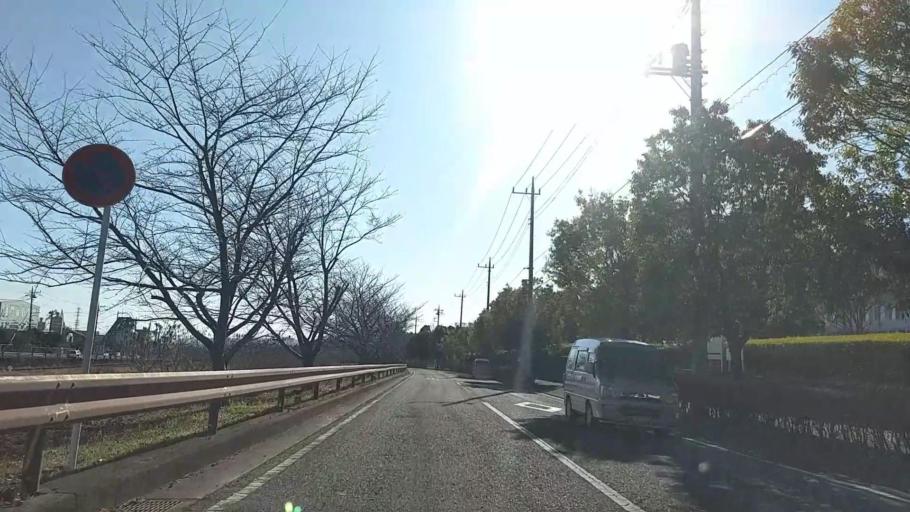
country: JP
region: Kanagawa
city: Hadano
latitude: 35.3887
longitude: 139.1865
